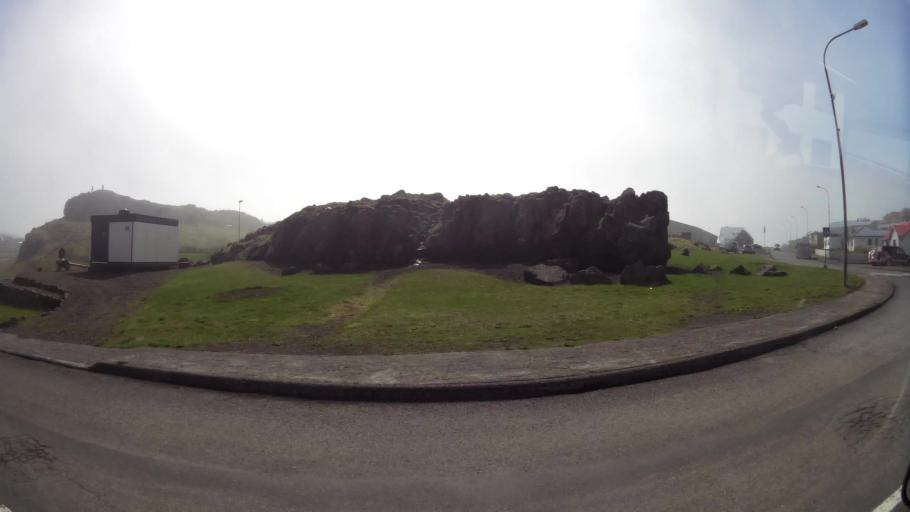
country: IS
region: East
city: Reydarfjoerdur
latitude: 64.6566
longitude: -14.2844
